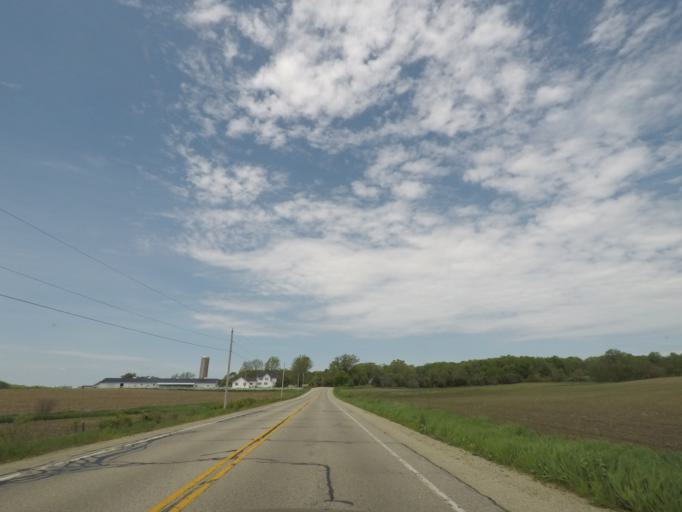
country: US
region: Wisconsin
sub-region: Rock County
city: Orfordville
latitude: 42.6370
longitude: -89.2717
